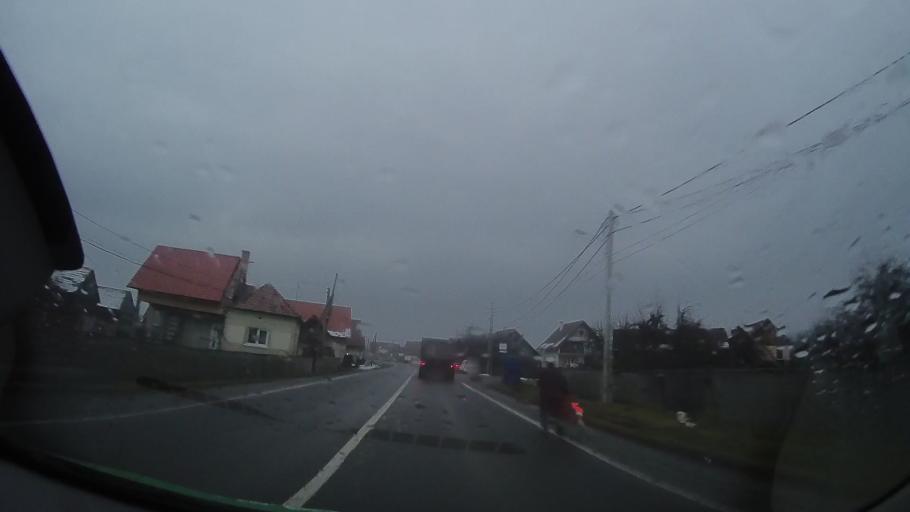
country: RO
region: Harghita
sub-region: Comuna Lazarea
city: Lazarea
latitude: 46.7550
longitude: 25.5191
